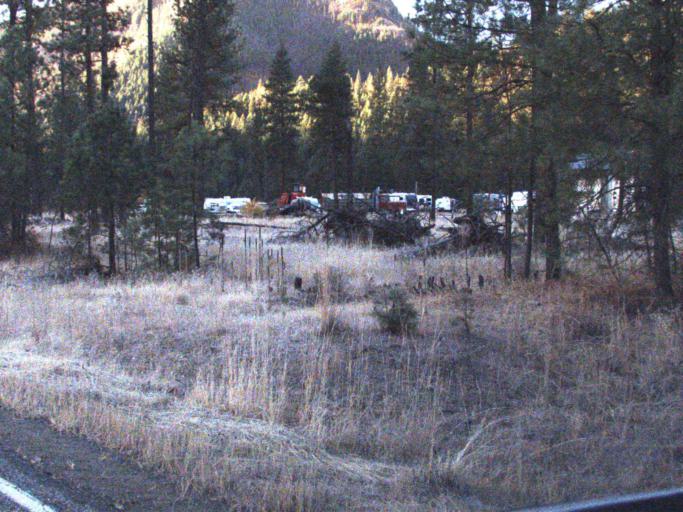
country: US
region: Washington
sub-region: Ferry County
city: Republic
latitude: 48.3101
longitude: -118.7383
